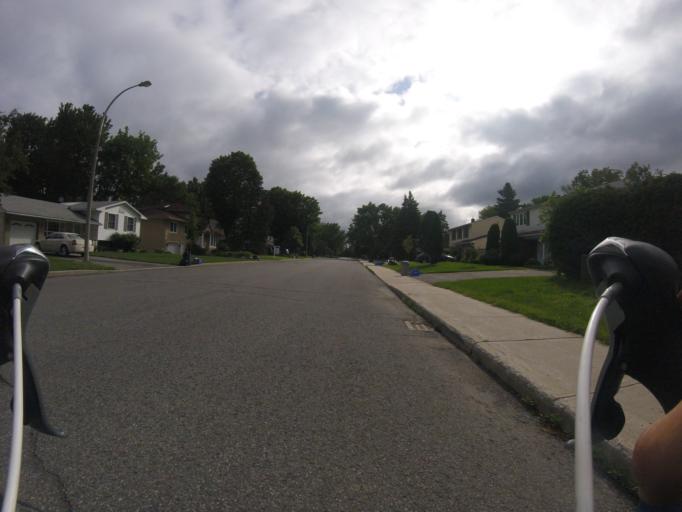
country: CA
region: Ontario
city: Bells Corners
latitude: 45.3392
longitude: -75.7791
